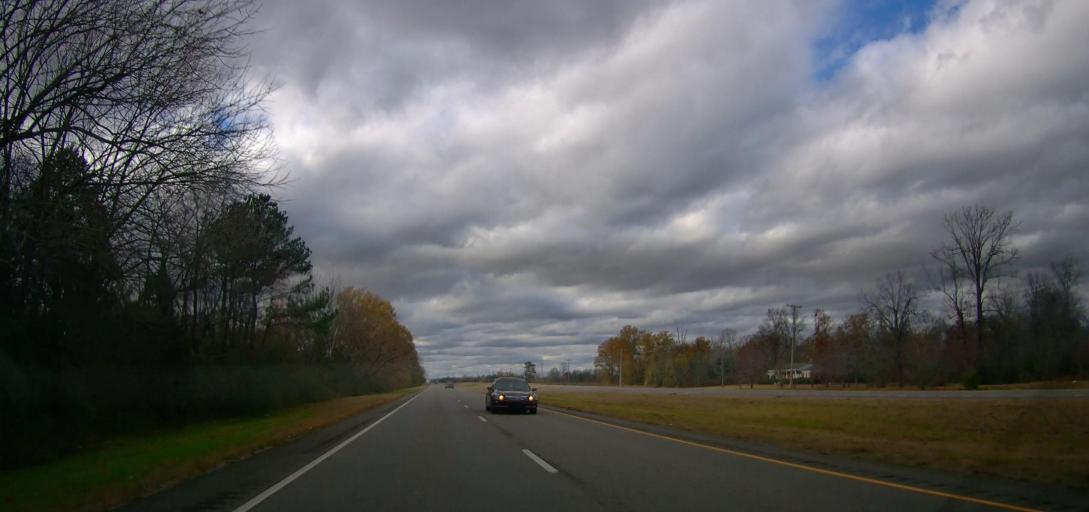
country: US
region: Alabama
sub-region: Morgan County
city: Danville
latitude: 34.3764
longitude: -87.0882
